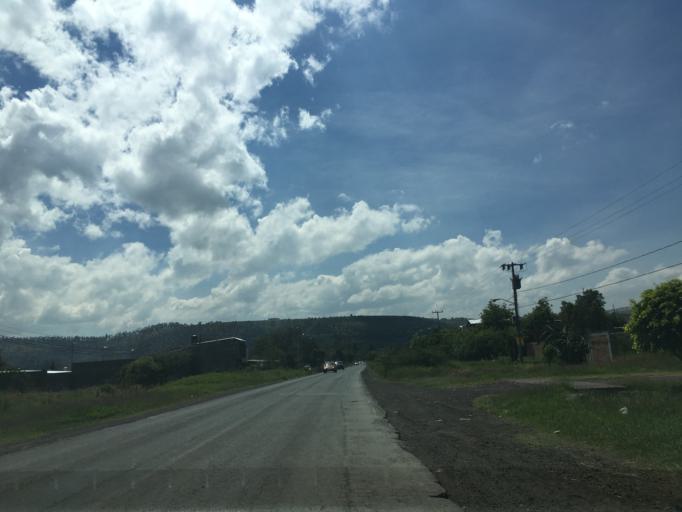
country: MX
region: Michoacan
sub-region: Morelia
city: La Mintzita (Piedra Dura)
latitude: 19.6552
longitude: -101.2796
